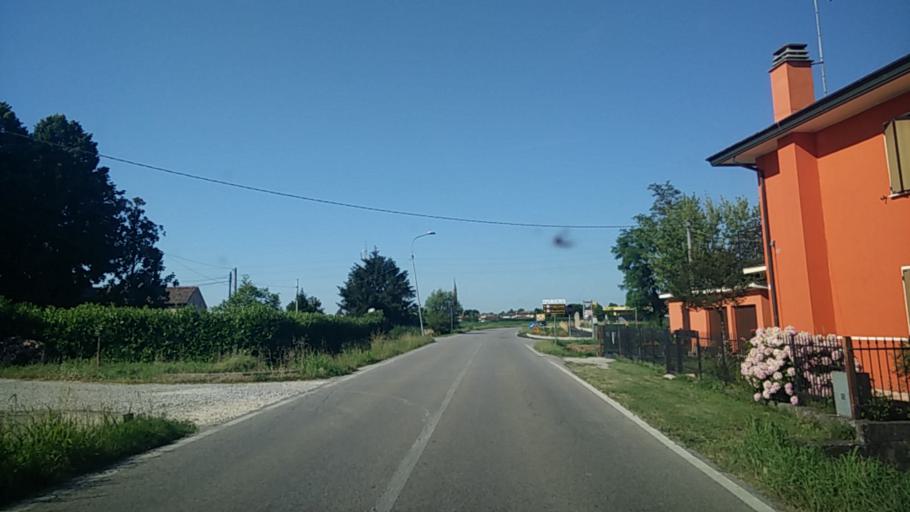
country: IT
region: Veneto
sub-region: Provincia di Venezia
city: Camponogara
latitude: 45.3945
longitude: 12.0790
